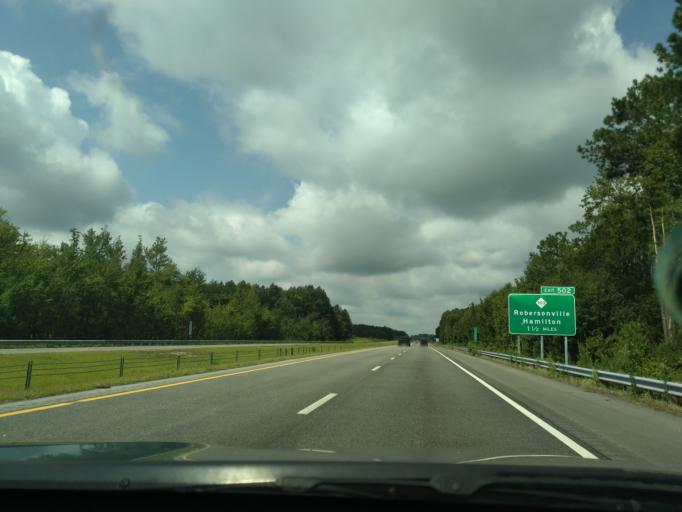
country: US
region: North Carolina
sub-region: Martin County
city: Robersonville
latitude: 35.8433
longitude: -77.2187
